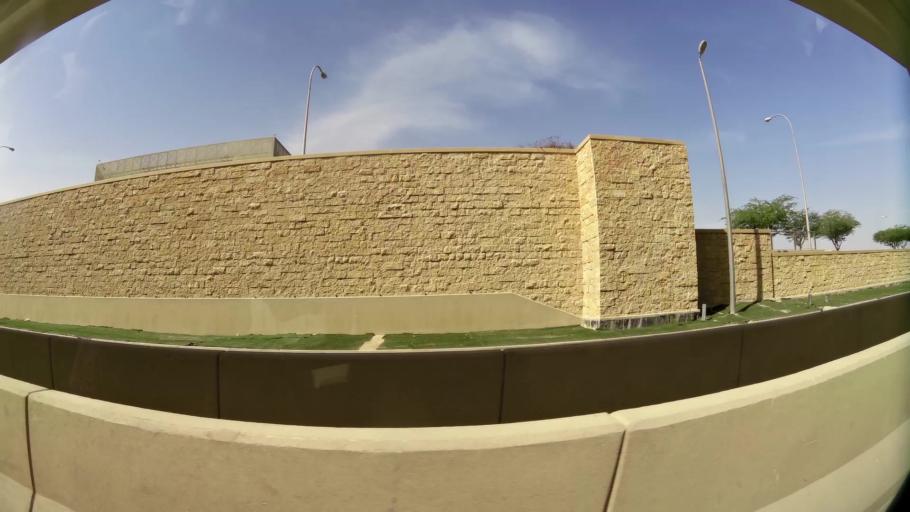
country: QA
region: Baladiyat ar Rayyan
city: Ar Rayyan
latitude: 25.3232
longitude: 51.4391
